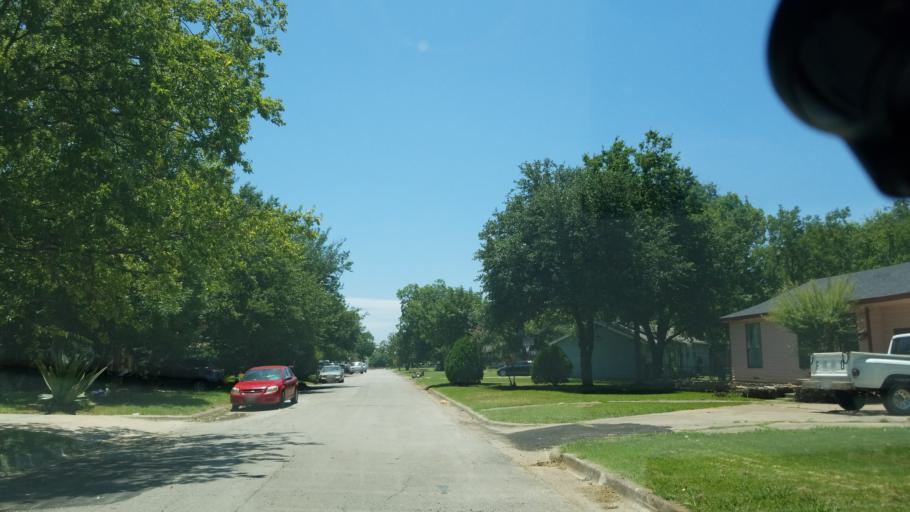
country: US
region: Texas
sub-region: Dallas County
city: Grand Prairie
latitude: 32.7520
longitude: -96.9522
